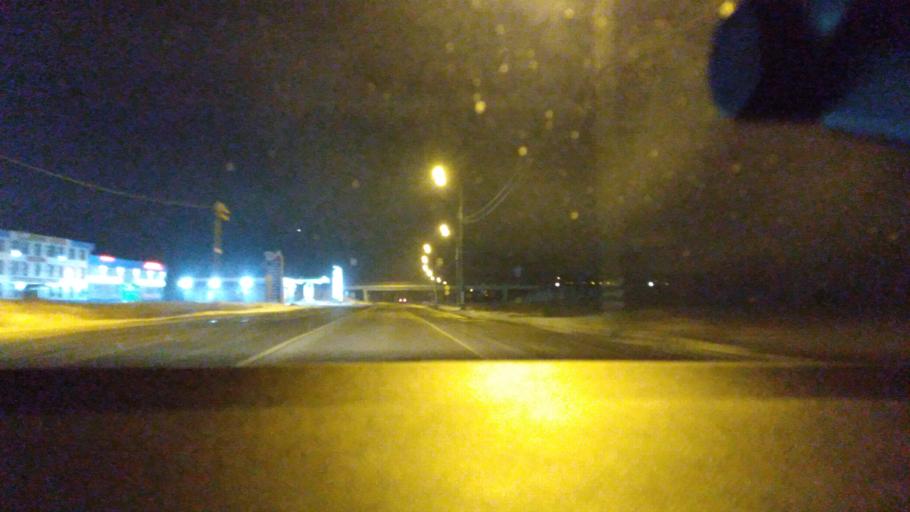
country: RU
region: Moskovskaya
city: Il'inskiy Pogost
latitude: 55.4891
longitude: 38.8763
